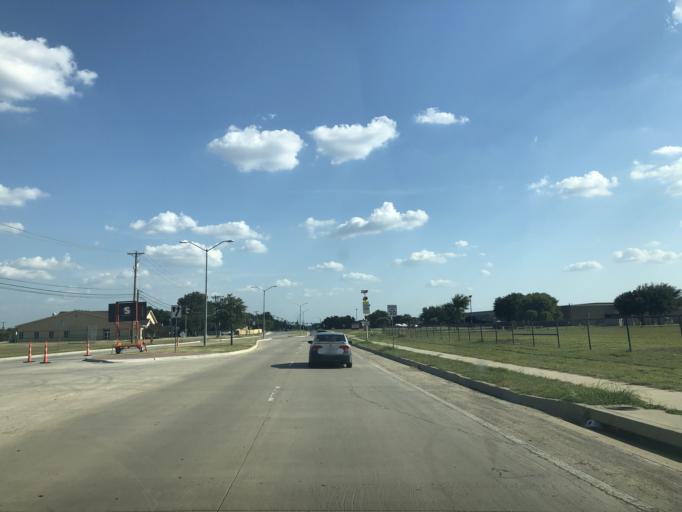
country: US
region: Texas
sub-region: Tarrant County
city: Saginaw
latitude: 32.8790
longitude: -97.3910
